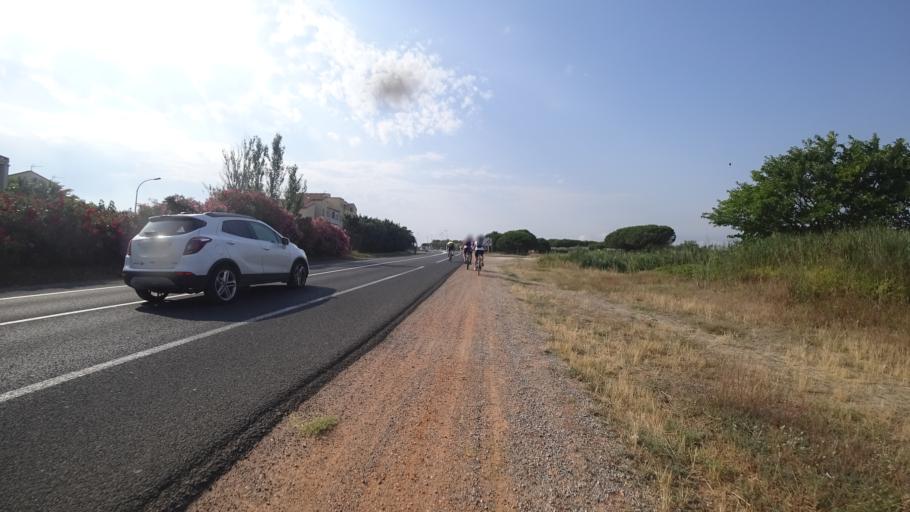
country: FR
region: Languedoc-Roussillon
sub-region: Departement des Pyrenees-Orientales
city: Canet-en-Roussillon
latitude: 42.6789
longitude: 3.0289
